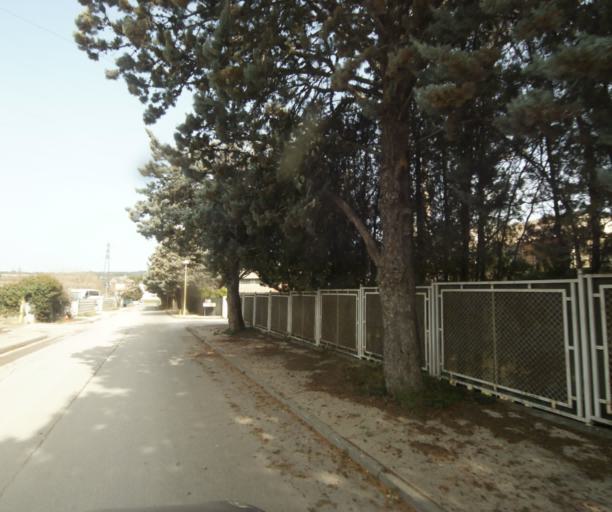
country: FR
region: Provence-Alpes-Cote d'Azur
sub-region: Departement des Bouches-du-Rhone
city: Gardanne
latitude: 43.4649
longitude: 5.4810
